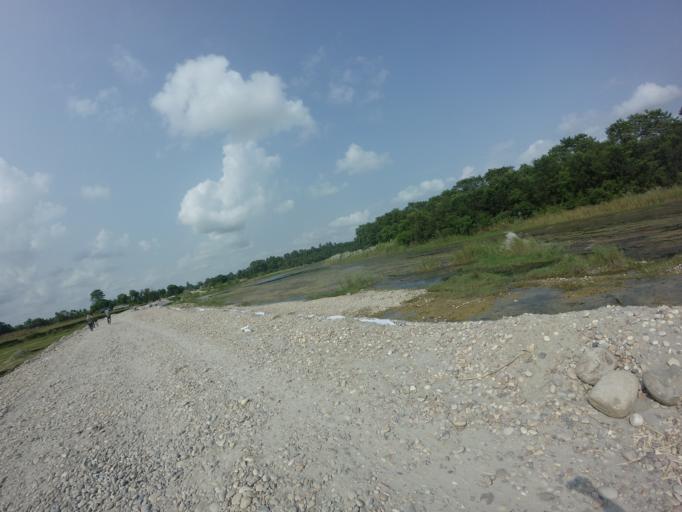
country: NP
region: Far Western
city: Tikapur
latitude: 28.4496
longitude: 81.0735
